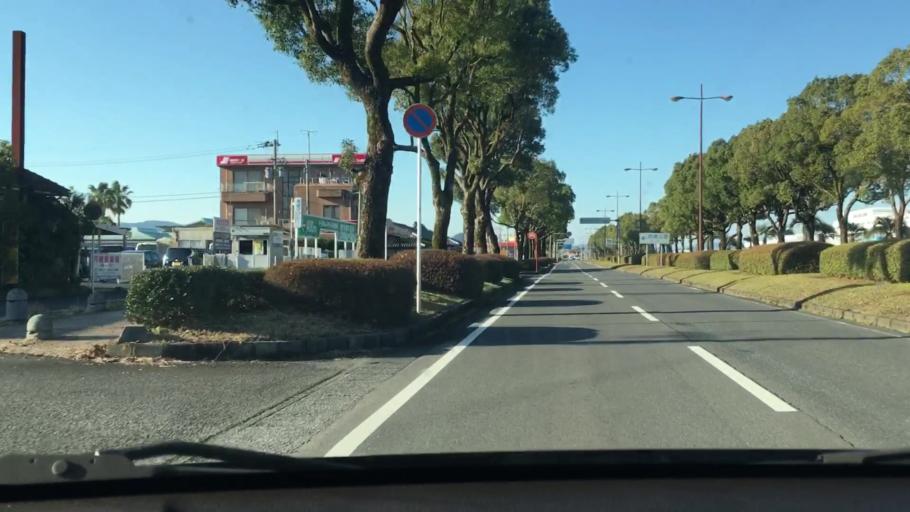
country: JP
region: Kagoshima
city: Kokubu-matsuki
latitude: 31.7975
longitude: 130.7167
